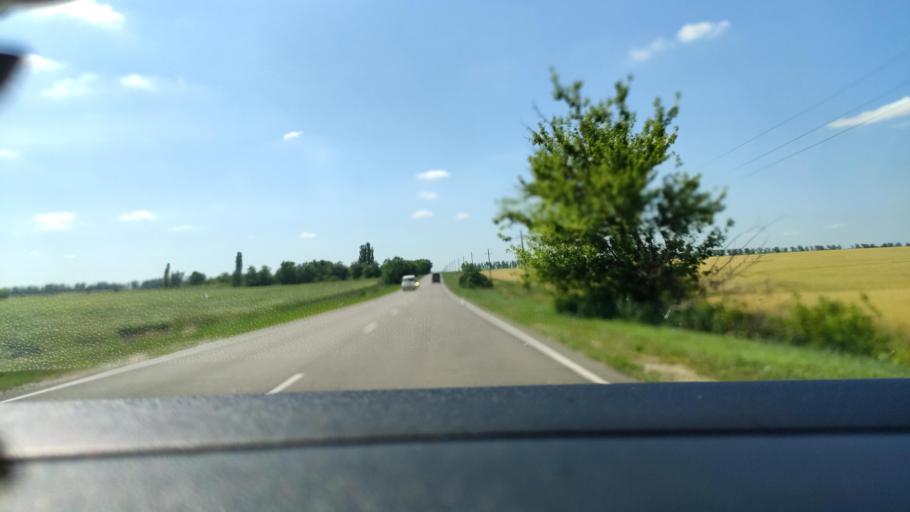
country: RU
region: Voronezj
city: Novaya Usman'
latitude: 51.5765
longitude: 39.3748
